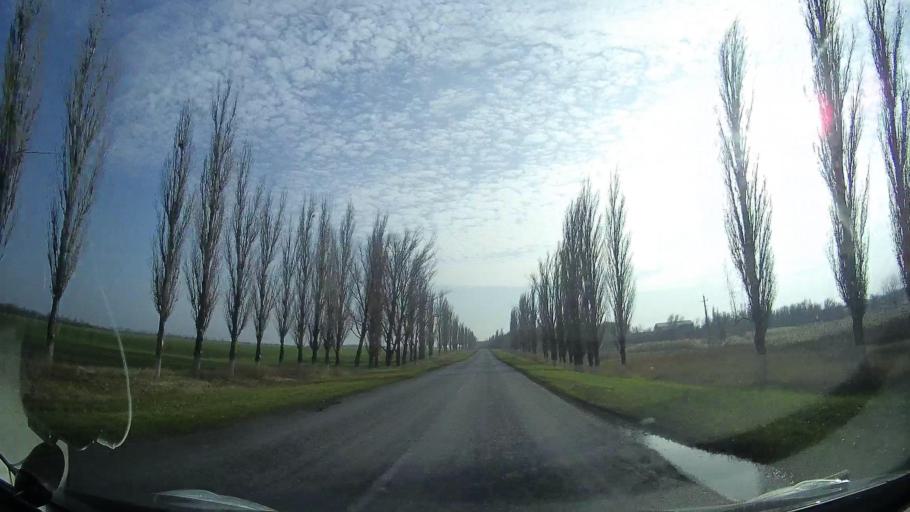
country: RU
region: Rostov
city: Mechetinskaya
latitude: 46.8304
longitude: 40.5514
